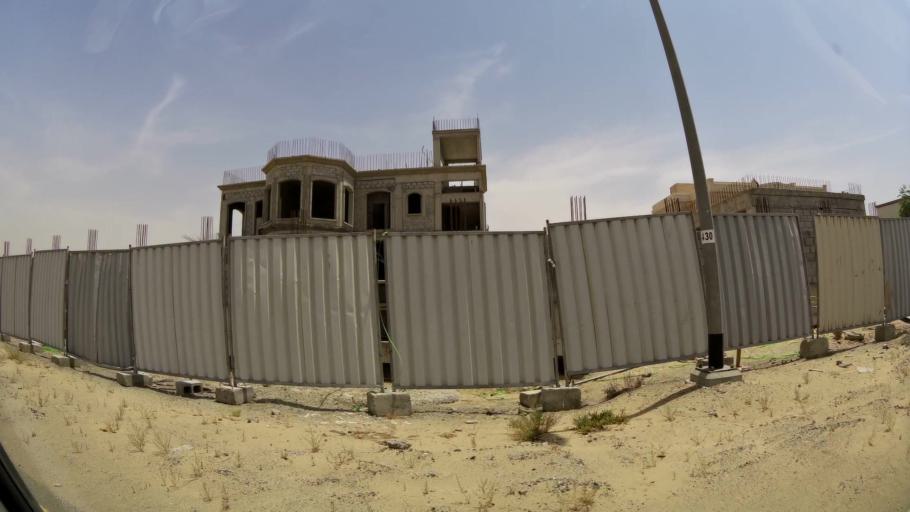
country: AE
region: Ash Shariqah
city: Sharjah
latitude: 25.2378
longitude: 55.4845
